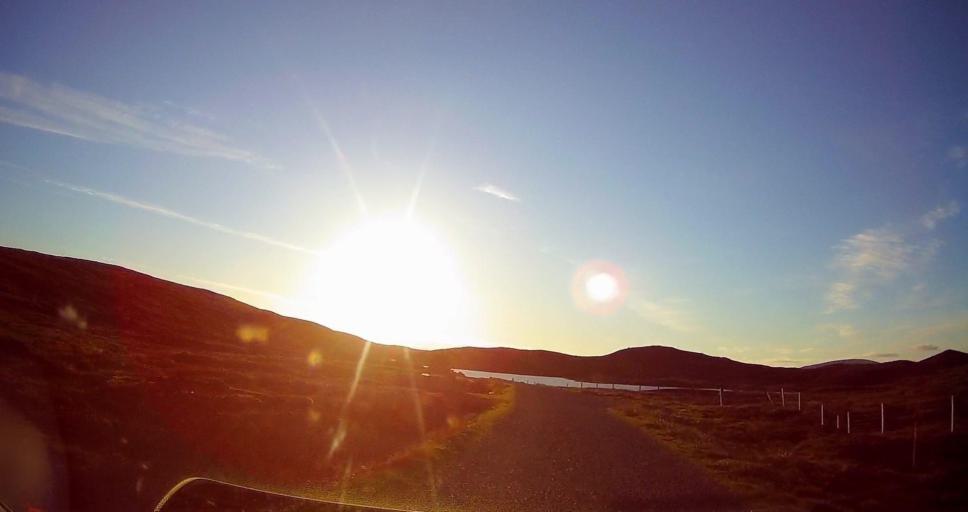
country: GB
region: Scotland
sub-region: Shetland Islands
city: Lerwick
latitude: 60.4420
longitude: -1.4031
